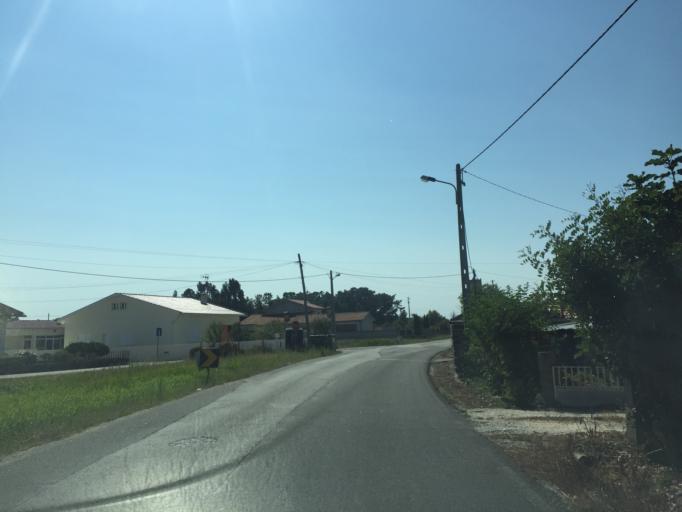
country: PT
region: Coimbra
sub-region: Montemor-O-Velho
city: Arazede
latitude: 40.3149
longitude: -8.7413
